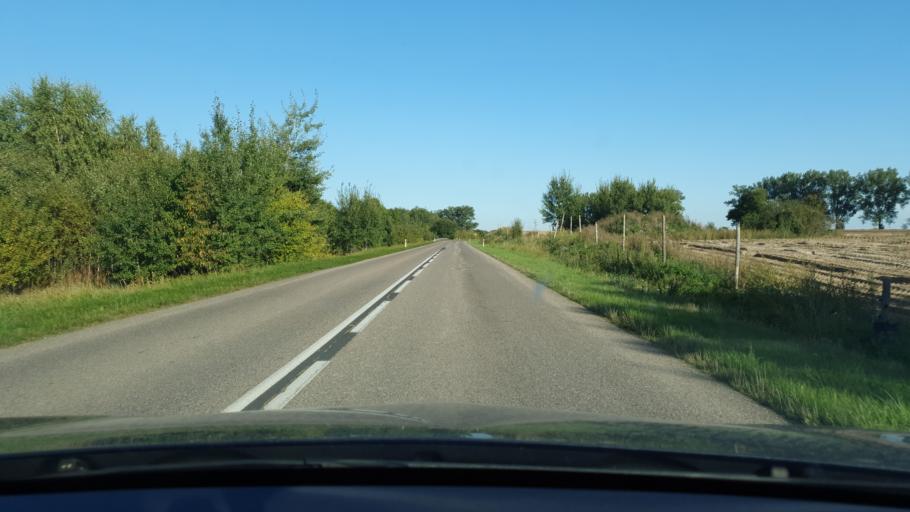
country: PL
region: West Pomeranian Voivodeship
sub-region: Powiat gryficki
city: Gryfice
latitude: 53.8164
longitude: 15.1525
